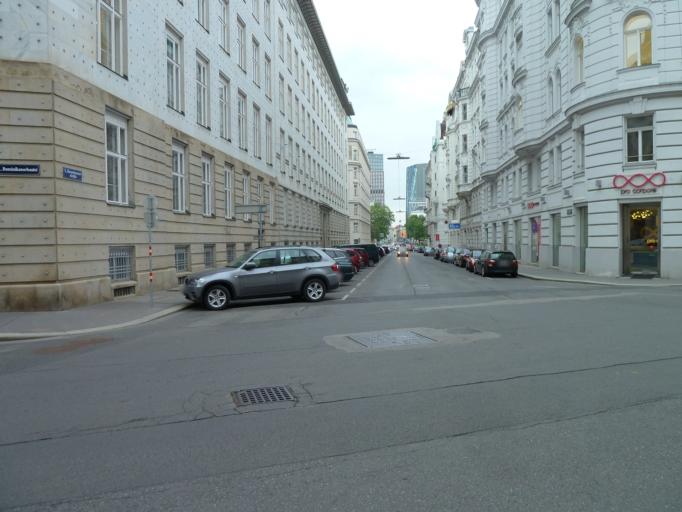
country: AT
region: Vienna
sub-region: Wien Stadt
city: Vienna
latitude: 48.2097
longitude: 16.3799
